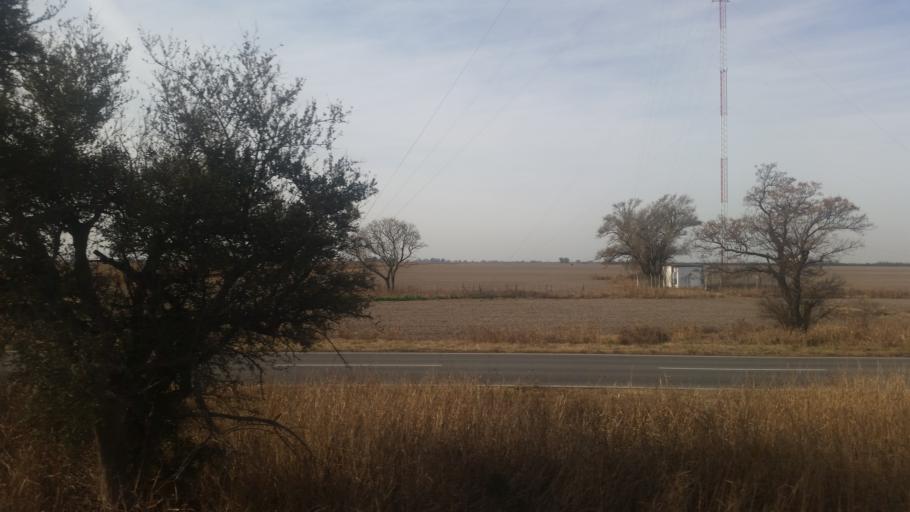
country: AR
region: Cordoba
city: Pilar
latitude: -31.7303
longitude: -63.8438
